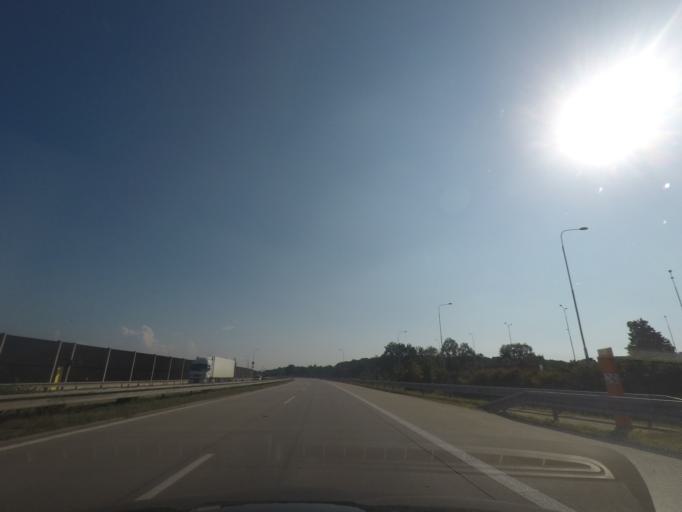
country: PL
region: Silesian Voivodeship
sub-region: Powiat raciborski
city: Chalupki
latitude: 49.9045
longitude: 18.3079
